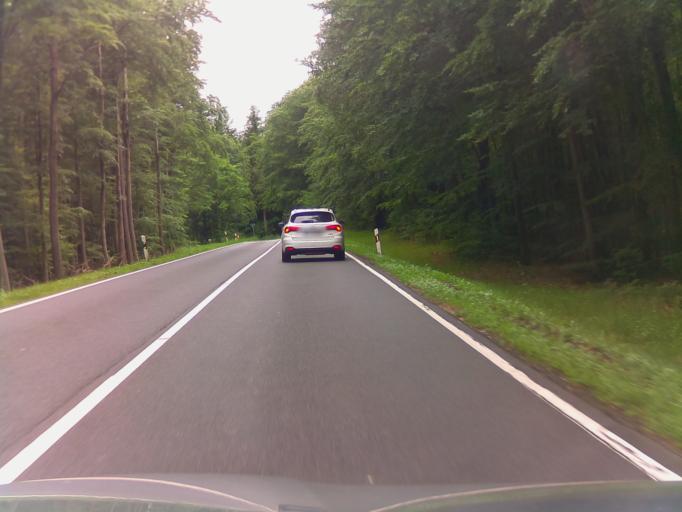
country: DE
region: Bavaria
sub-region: Regierungsbezirk Unterfranken
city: Rothenbuch
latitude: 49.9677
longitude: 9.3602
